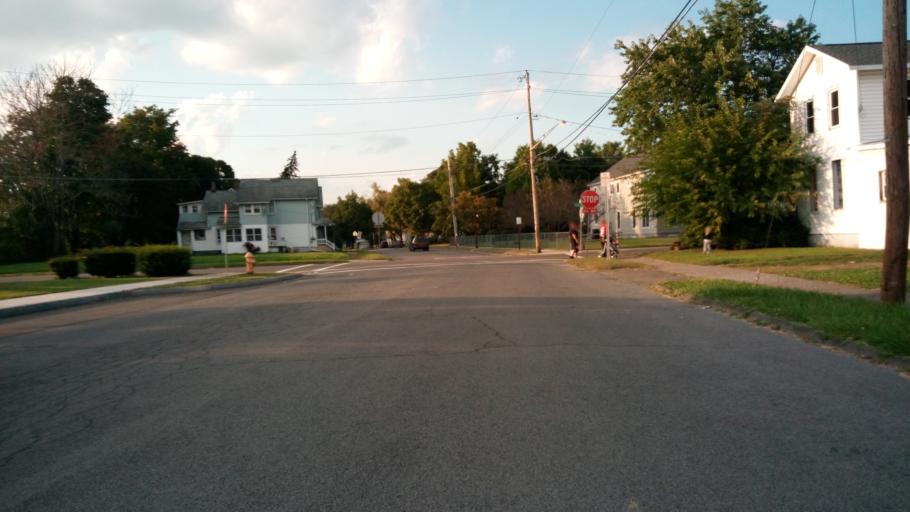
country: US
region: New York
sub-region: Chemung County
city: Elmira
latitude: 42.1071
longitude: -76.8069
